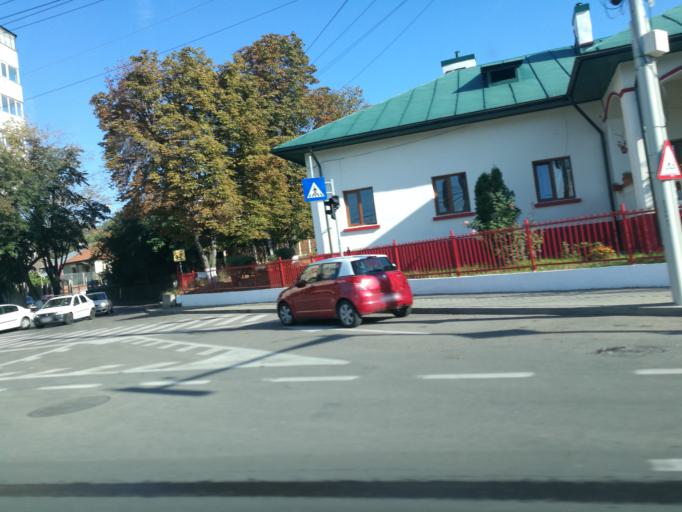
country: RO
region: Iasi
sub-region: Municipiul Iasi
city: Iasi
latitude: 47.1734
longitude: 27.5608
